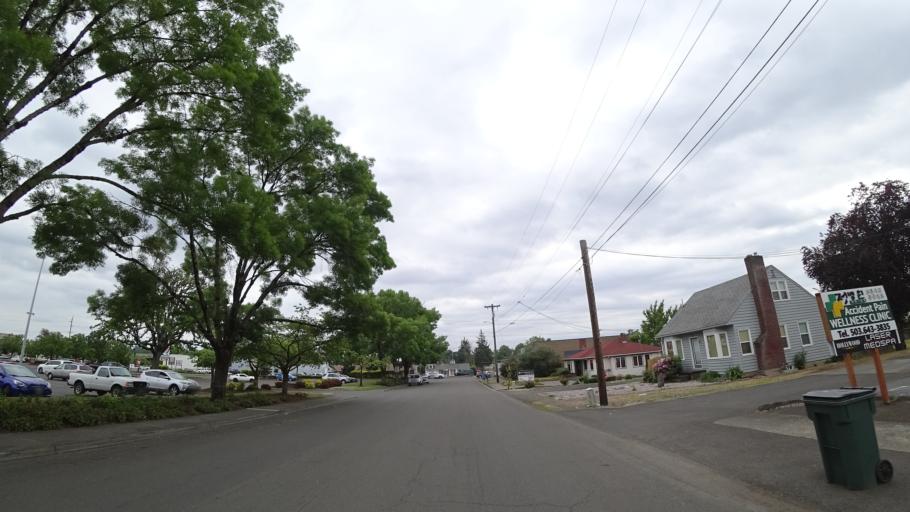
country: US
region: Oregon
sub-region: Washington County
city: Beaverton
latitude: 45.4875
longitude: -122.7889
